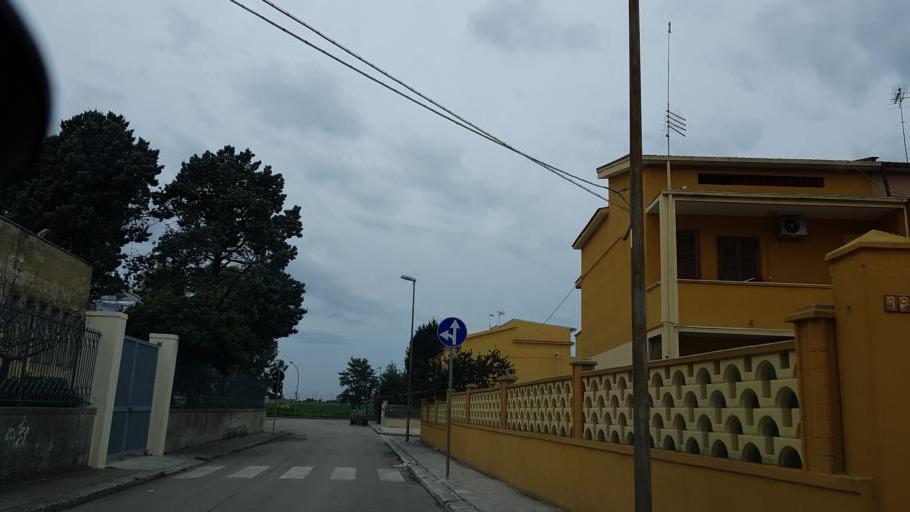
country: IT
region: Apulia
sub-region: Provincia di Brindisi
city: La Rosa
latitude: 40.6096
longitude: 17.9518
